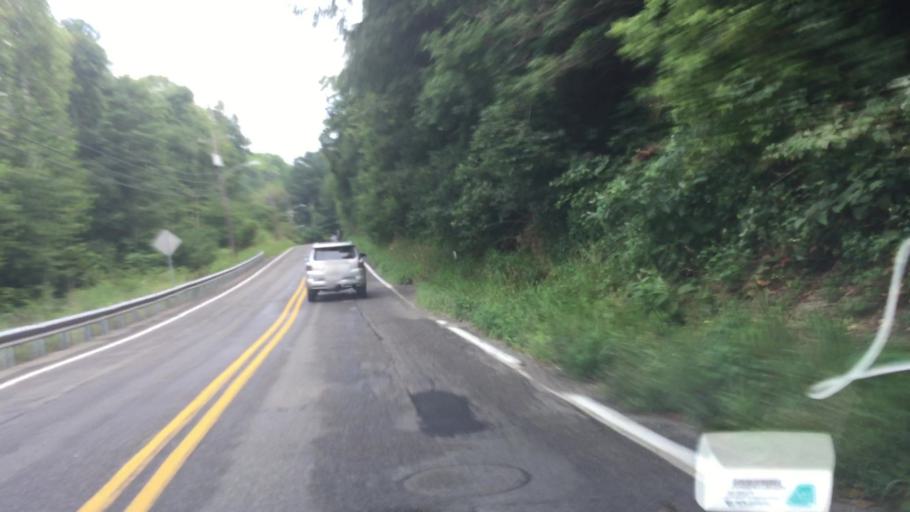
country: US
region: Pennsylvania
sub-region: Allegheny County
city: Heidelberg
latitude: 40.3816
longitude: -80.0894
